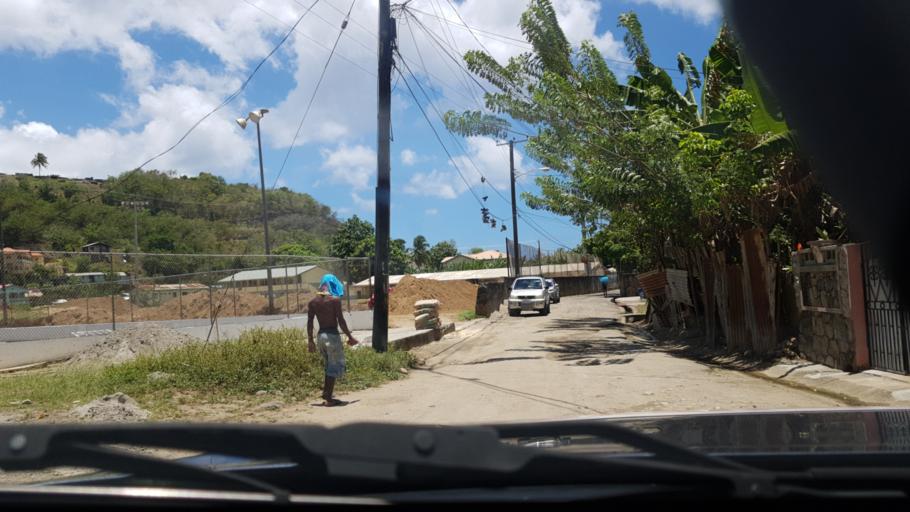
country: LC
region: Anse-la-Raye
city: Canaries
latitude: 13.9033
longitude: -61.0656
